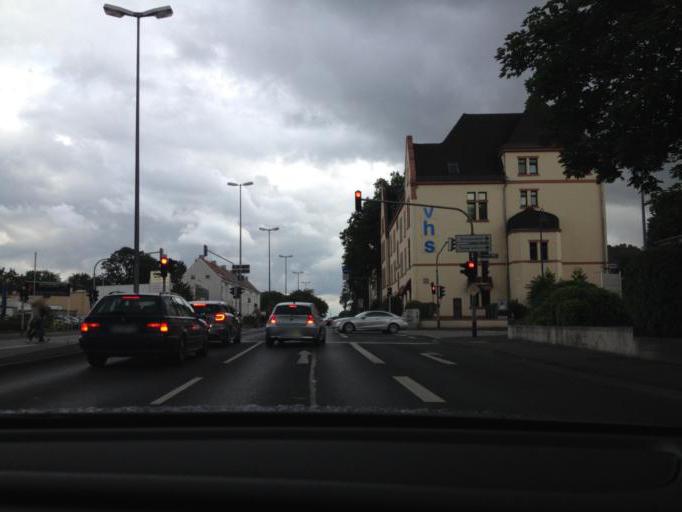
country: DE
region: Hesse
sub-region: Regierungsbezirk Darmstadt
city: Wiesbaden
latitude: 50.0700
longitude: 8.2265
